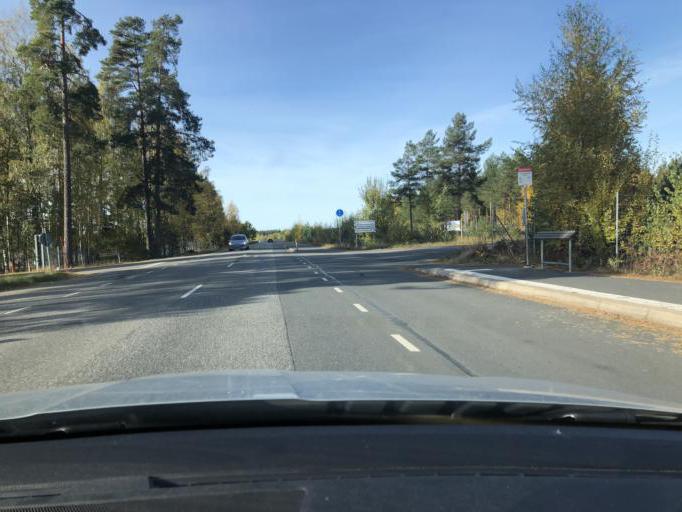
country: SE
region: Joenkoeping
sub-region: Jonkopings Kommun
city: Jonkoping
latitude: 57.7722
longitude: 14.0898
